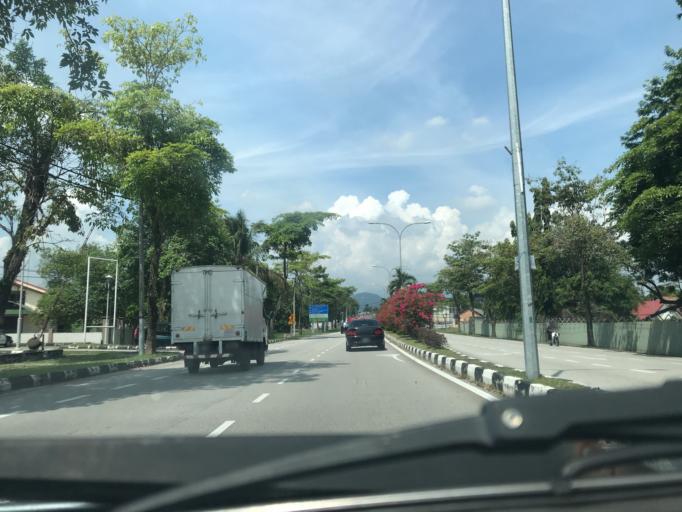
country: MY
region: Perak
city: Ipoh
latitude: 4.6021
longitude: 101.1021
